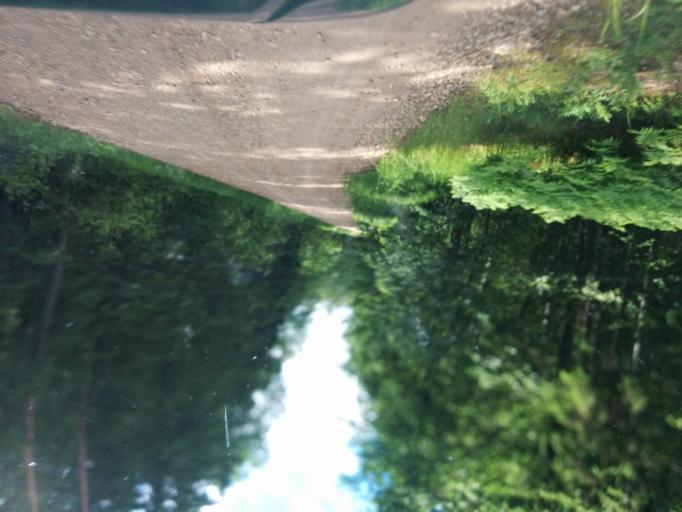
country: LV
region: Vilaka
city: Vilaka
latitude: 57.3711
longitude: 27.6585
